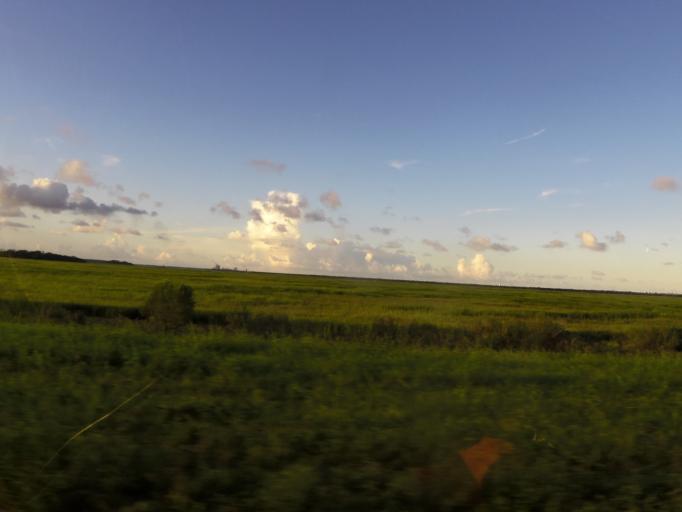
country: US
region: Georgia
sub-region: Glynn County
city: Brunswick
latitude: 31.1121
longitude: -81.5258
